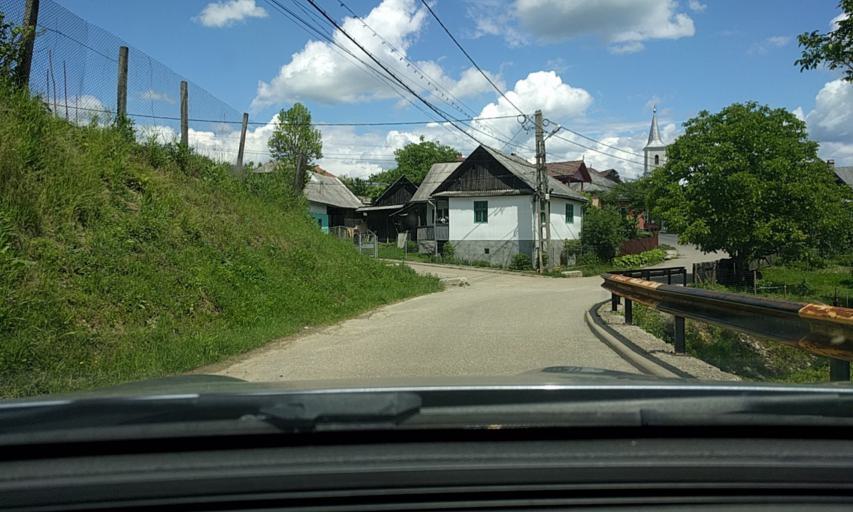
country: RO
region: Bistrita-Nasaud
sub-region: Oras Nasaud
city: Nasaud
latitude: 47.2778
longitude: 24.4045
